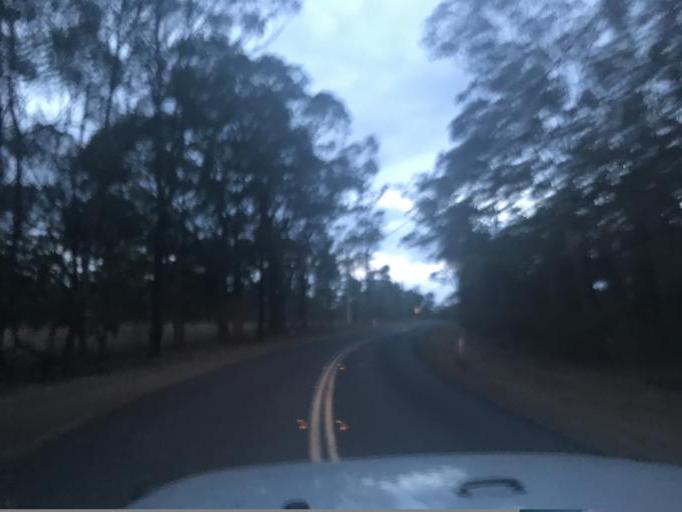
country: AU
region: New South Wales
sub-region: Hawkesbury
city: Pitt Town
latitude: -33.4617
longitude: 150.8502
